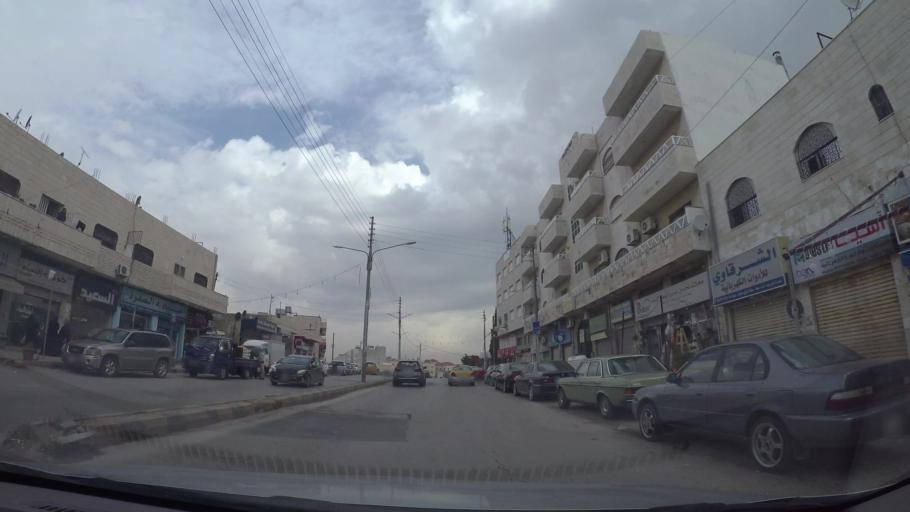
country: JO
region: Amman
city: Umm as Summaq
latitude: 31.9021
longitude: 35.8457
